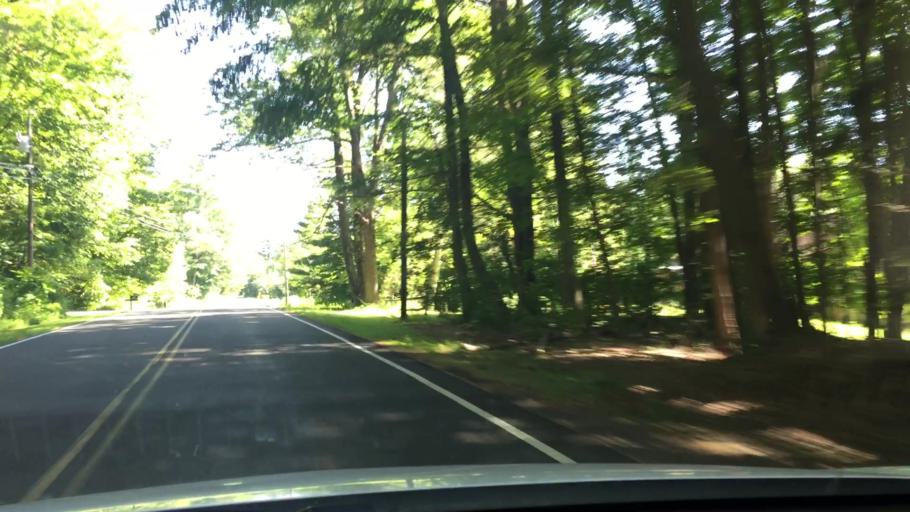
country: US
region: Massachusetts
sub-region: Berkshire County
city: Richmond
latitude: 42.3690
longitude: -73.3477
